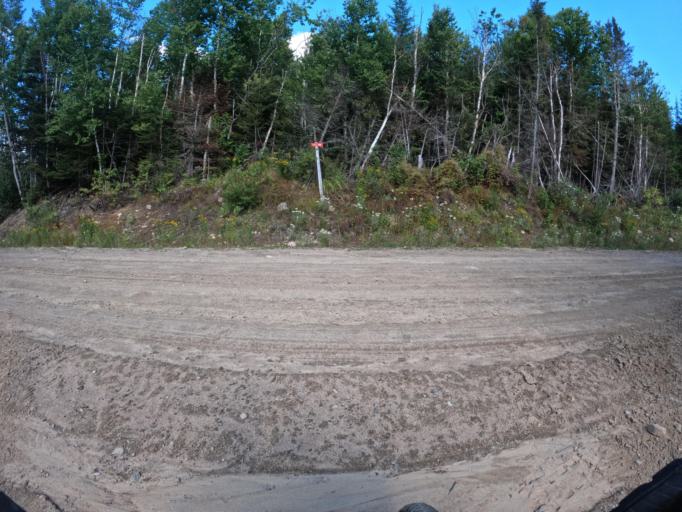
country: CA
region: Quebec
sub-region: Capitale-Nationale
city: La Malbaie
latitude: 47.9144
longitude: -70.3158
